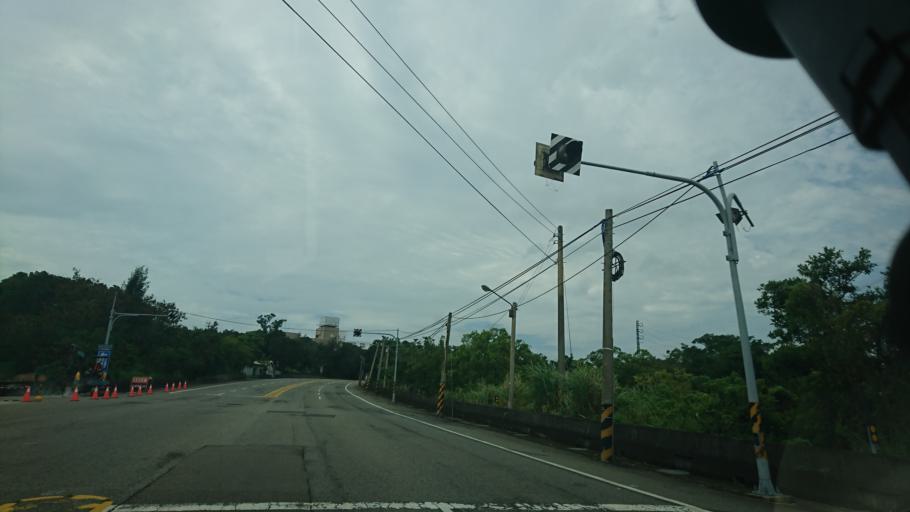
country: TW
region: Taiwan
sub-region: Miaoli
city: Miaoli
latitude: 24.5165
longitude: 120.7876
